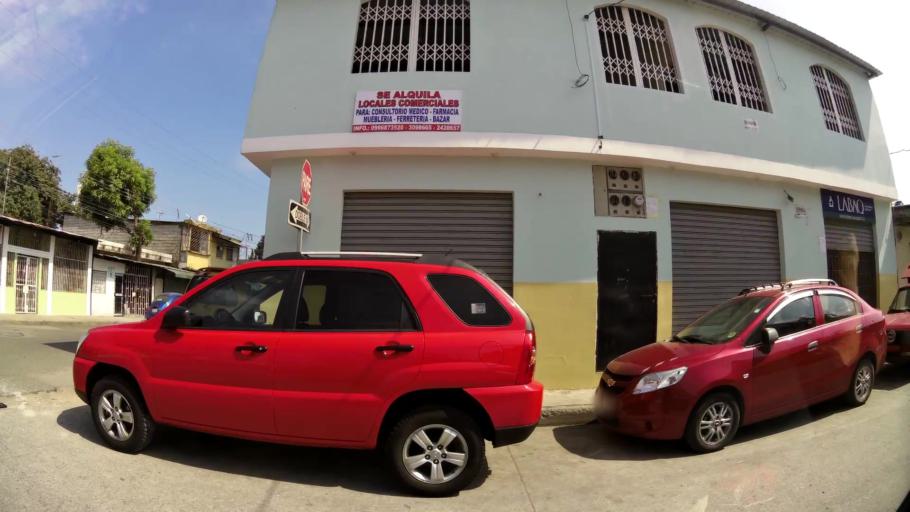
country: EC
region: Guayas
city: Guayaquil
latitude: -2.2763
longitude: -79.8779
